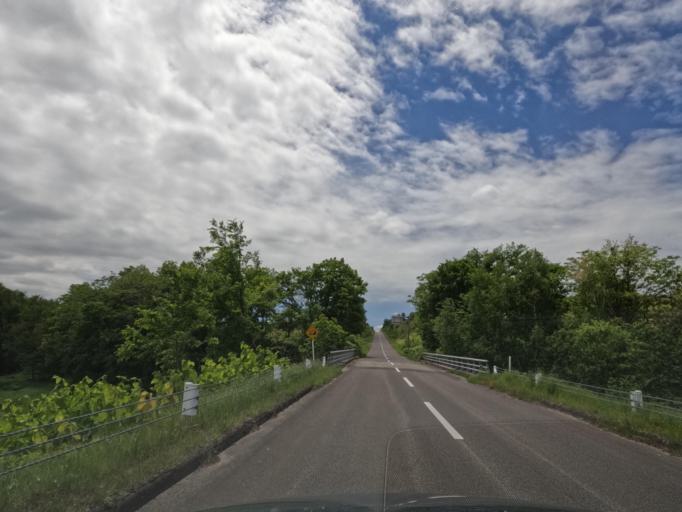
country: JP
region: Hokkaido
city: Shimo-furano
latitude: 43.5134
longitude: 142.4242
